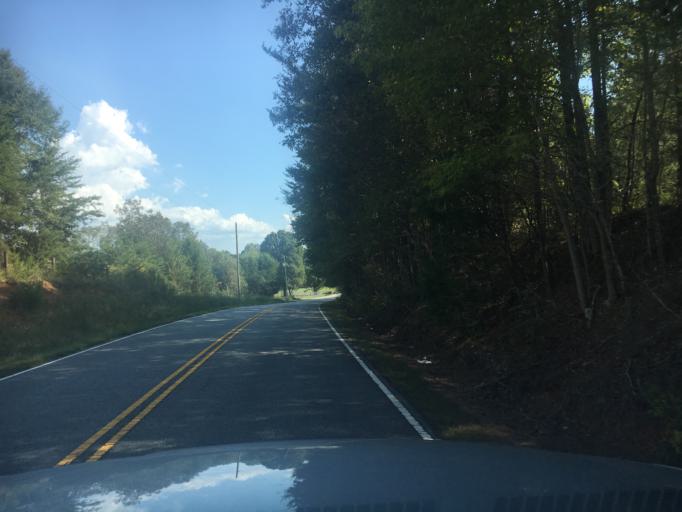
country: US
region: South Carolina
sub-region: Pickens County
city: Liberty
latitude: 34.7251
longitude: -82.6392
